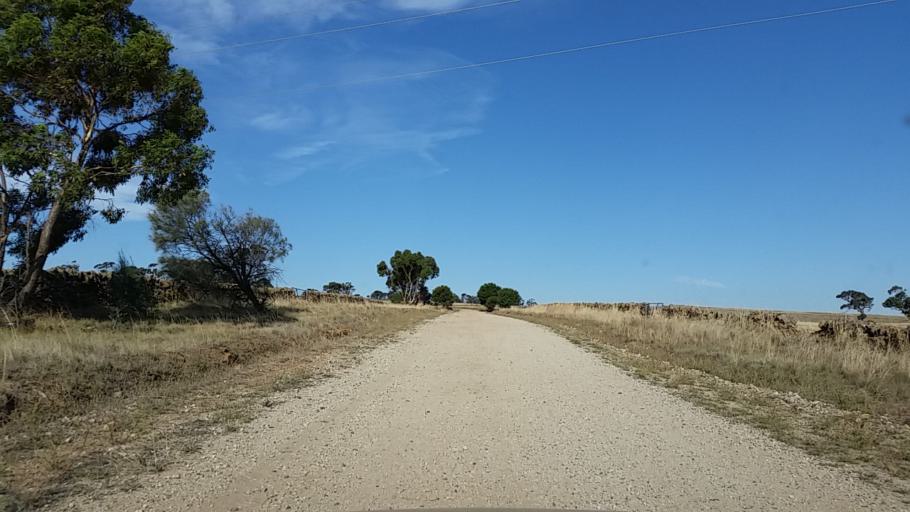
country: AU
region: South Australia
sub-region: Barossa
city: Angaston
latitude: -34.6112
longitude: 139.1838
